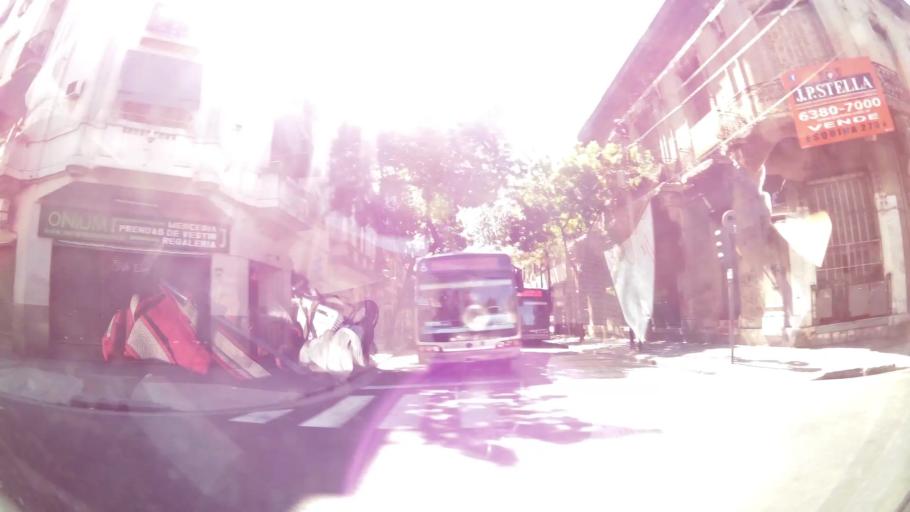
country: AR
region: Buenos Aires F.D.
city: Buenos Aires
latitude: -34.6247
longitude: -58.3844
